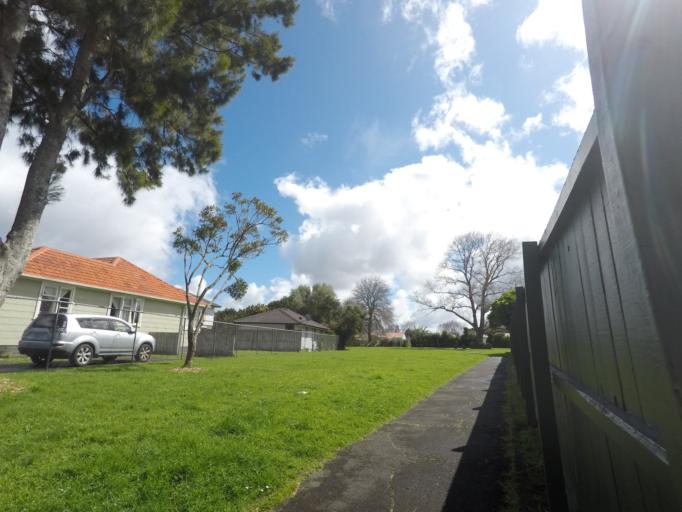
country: NZ
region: Auckland
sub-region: Auckland
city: Rosebank
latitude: -36.8905
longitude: 174.6811
